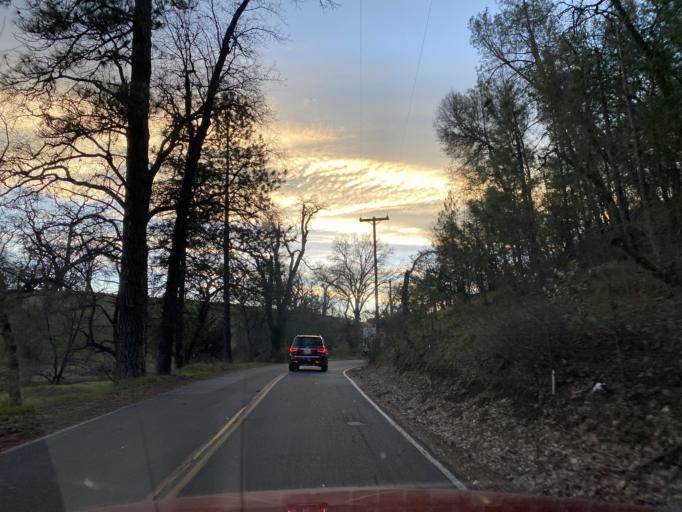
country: US
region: California
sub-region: Amador County
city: Plymouth
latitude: 38.5082
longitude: -120.7688
